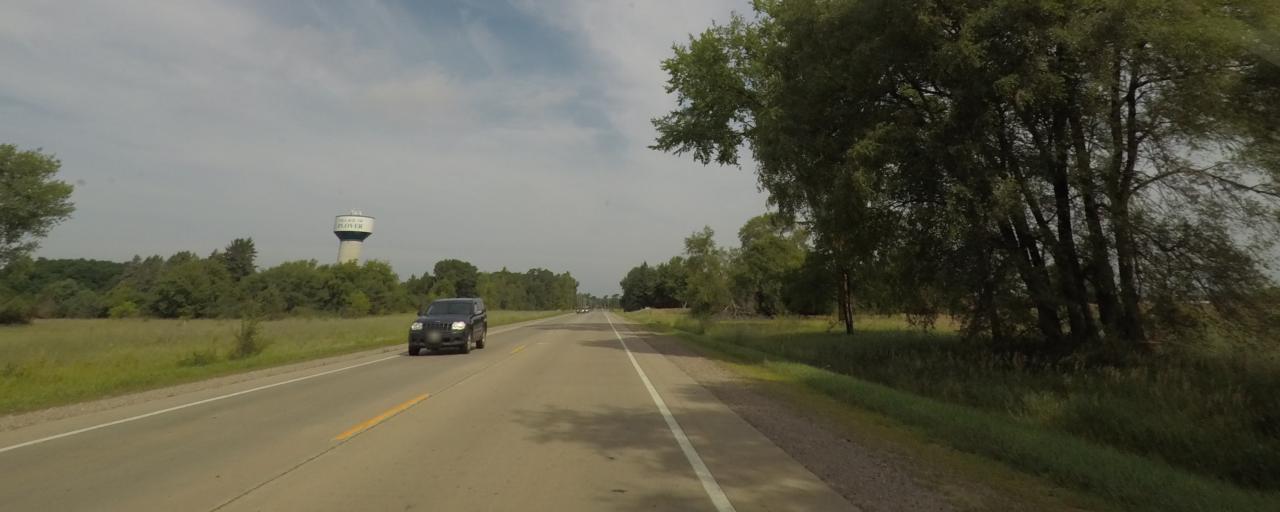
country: US
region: Wisconsin
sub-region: Portage County
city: Plover
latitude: 44.4410
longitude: -89.5336
